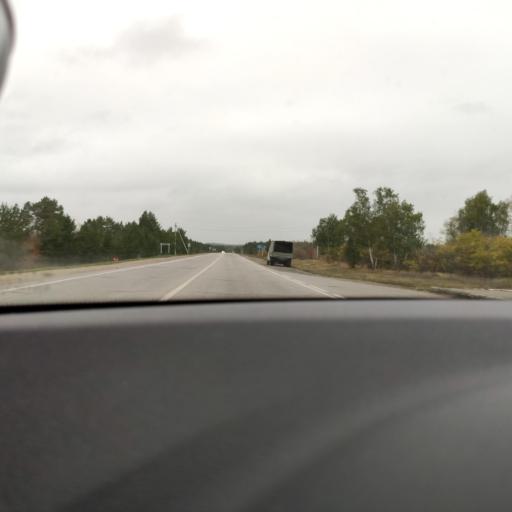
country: RU
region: Samara
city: Mirnyy
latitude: 53.5244
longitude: 50.3169
